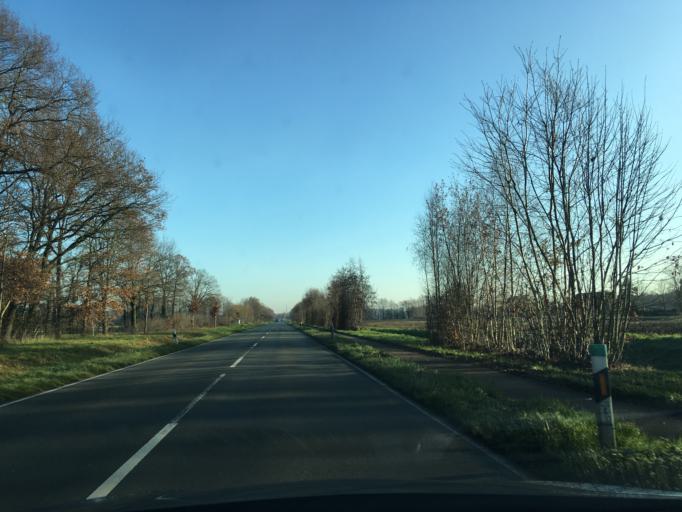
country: DE
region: North Rhine-Westphalia
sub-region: Regierungsbezirk Munster
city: Ahaus
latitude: 52.1169
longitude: 6.9386
